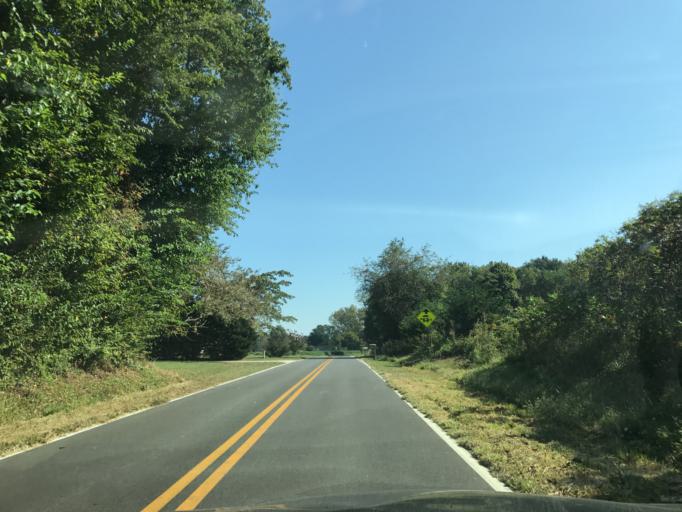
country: US
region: Maryland
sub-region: Queen Anne's County
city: Kingstown
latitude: 39.2529
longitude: -76.0037
